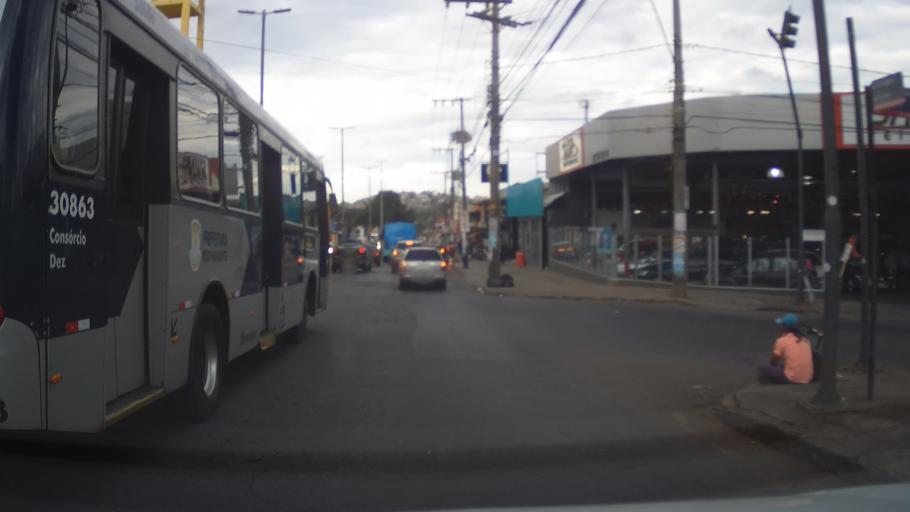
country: BR
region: Minas Gerais
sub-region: Contagem
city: Contagem
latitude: -19.9612
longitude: -44.0159
